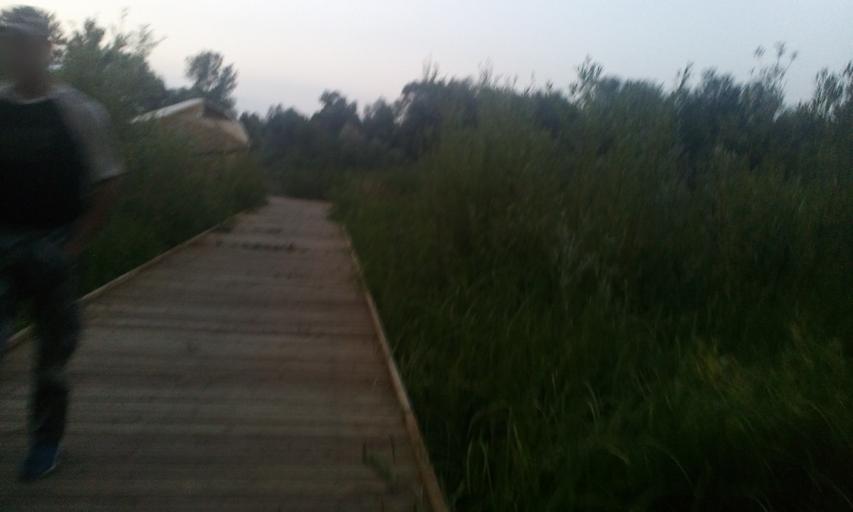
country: PL
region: Lesser Poland Voivodeship
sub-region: Powiat nowosadecki
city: Stary Sacz
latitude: 49.5842
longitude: 20.6444
